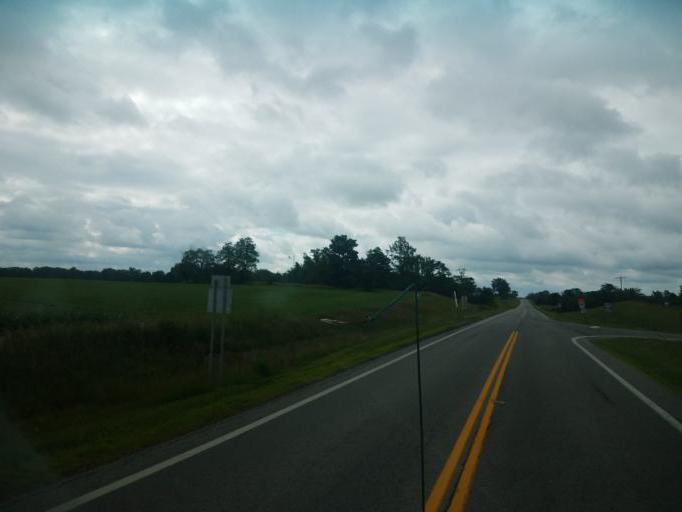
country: US
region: Ohio
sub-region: Logan County
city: Northwood
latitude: 40.3842
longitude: -83.6044
